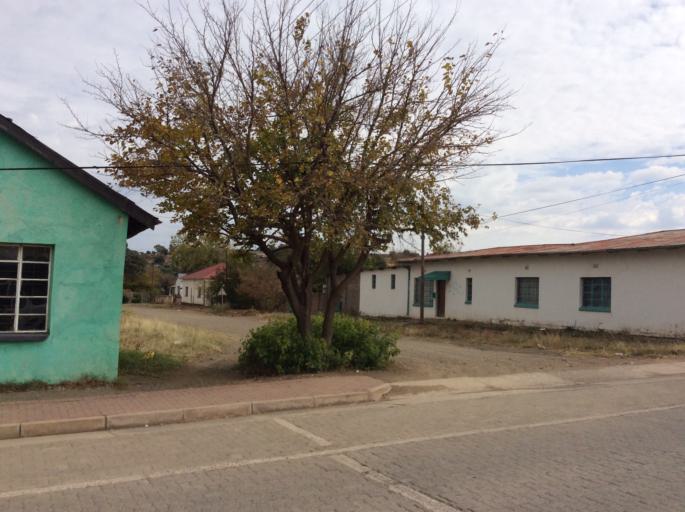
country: LS
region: Mafeteng
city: Mafeteng
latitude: -29.7255
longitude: 27.0390
